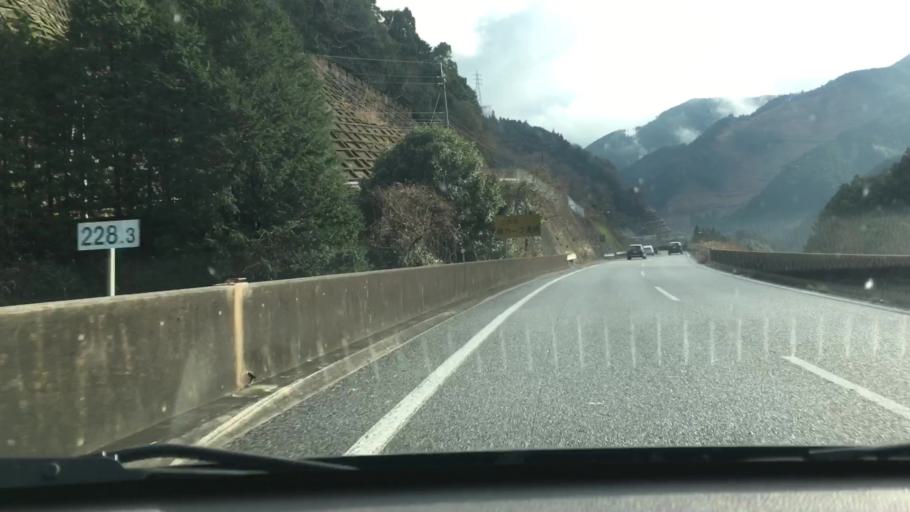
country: JP
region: Kumamoto
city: Yatsushiro
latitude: 32.4093
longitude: 130.6967
